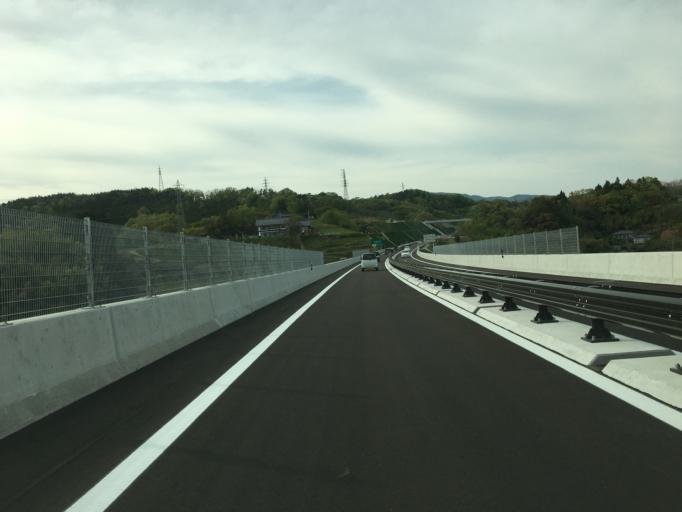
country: JP
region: Fukushima
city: Hobaramachi
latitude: 37.7994
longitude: 140.5440
